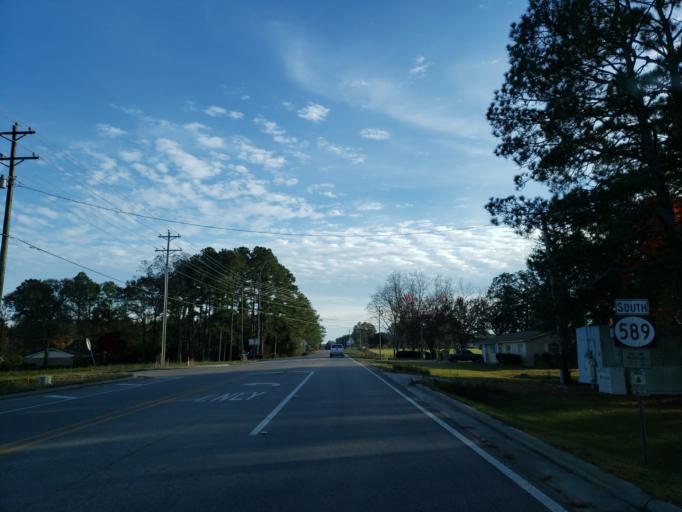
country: US
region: Mississippi
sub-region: Lamar County
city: West Hattiesburg
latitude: 31.3116
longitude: -89.4718
